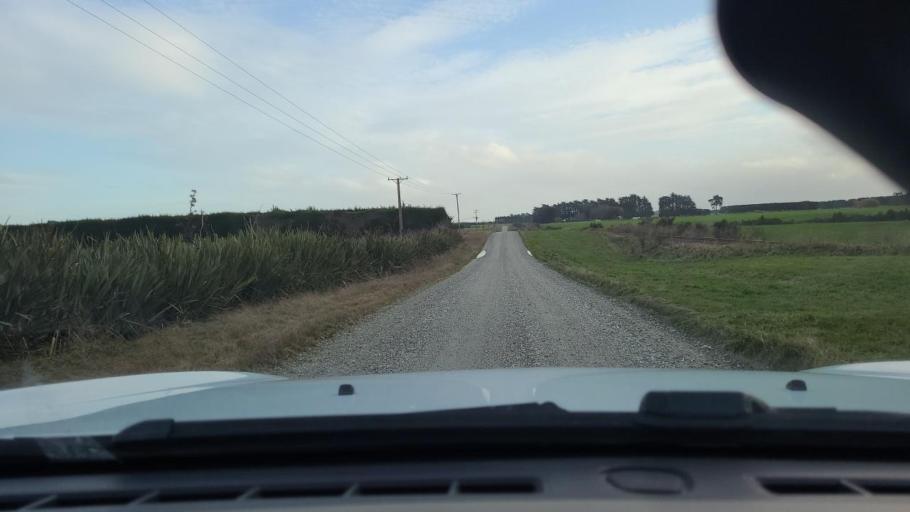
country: NZ
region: Southland
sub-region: Gore District
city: Gore
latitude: -46.3328
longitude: 168.6916
